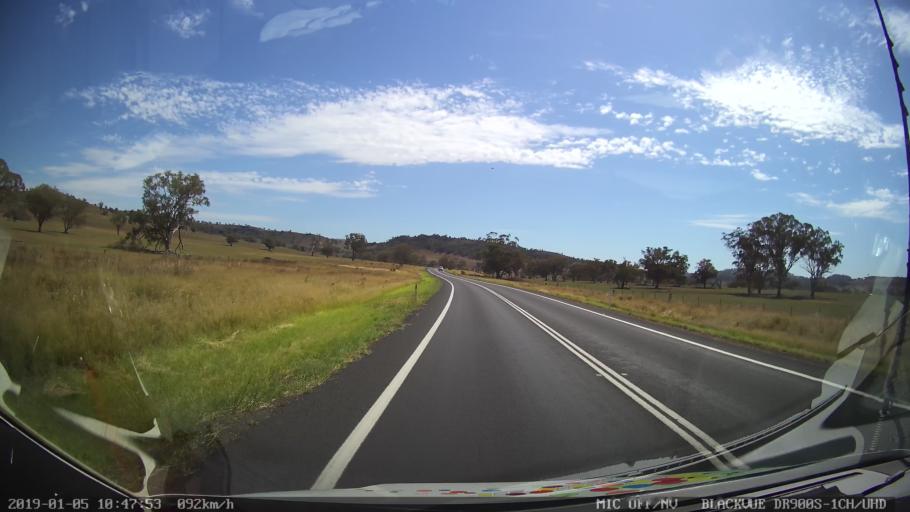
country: AU
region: New South Wales
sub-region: Warrumbungle Shire
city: Coonabarabran
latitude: -31.4411
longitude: 149.0389
